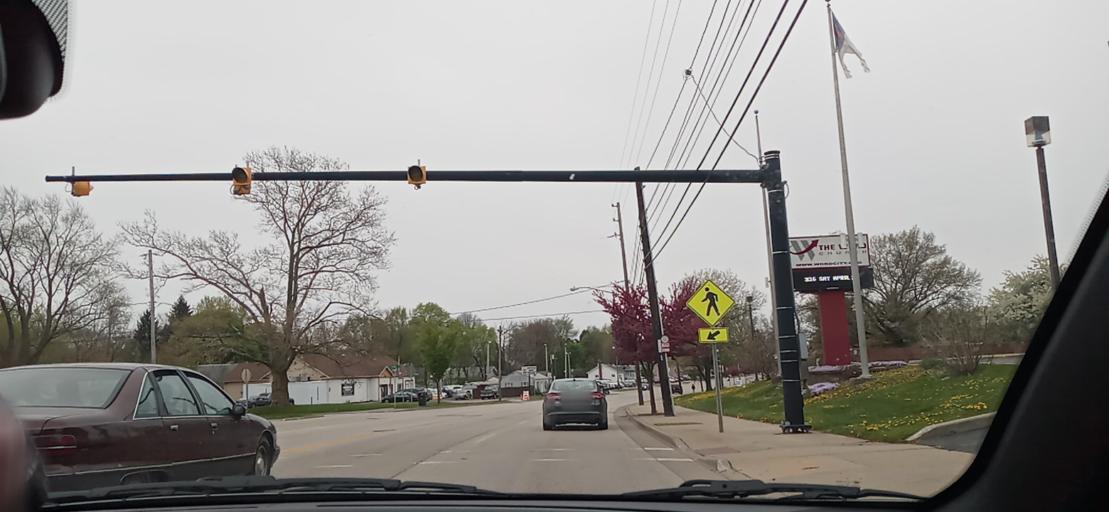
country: US
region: Ohio
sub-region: Summit County
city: Portage Lakes
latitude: 41.0356
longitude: -81.5454
